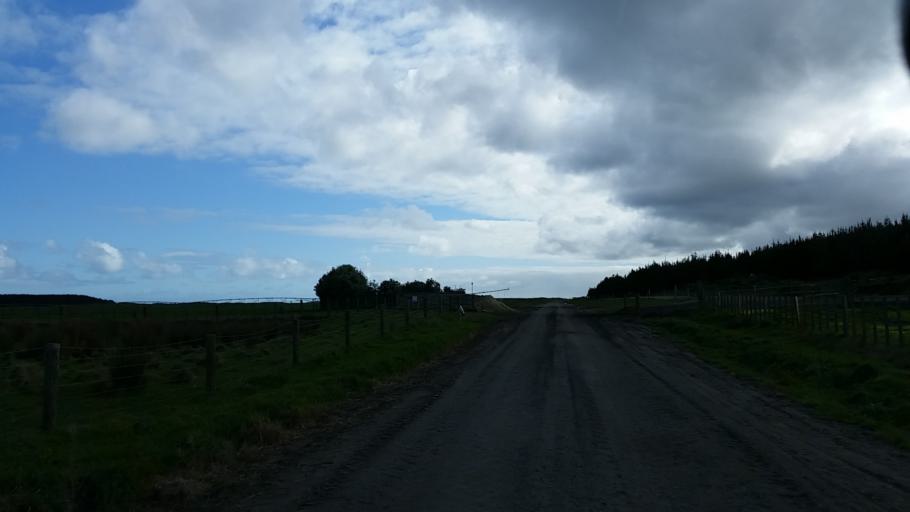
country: NZ
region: Taranaki
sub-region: South Taranaki District
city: Patea
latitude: -39.7988
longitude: 174.5947
